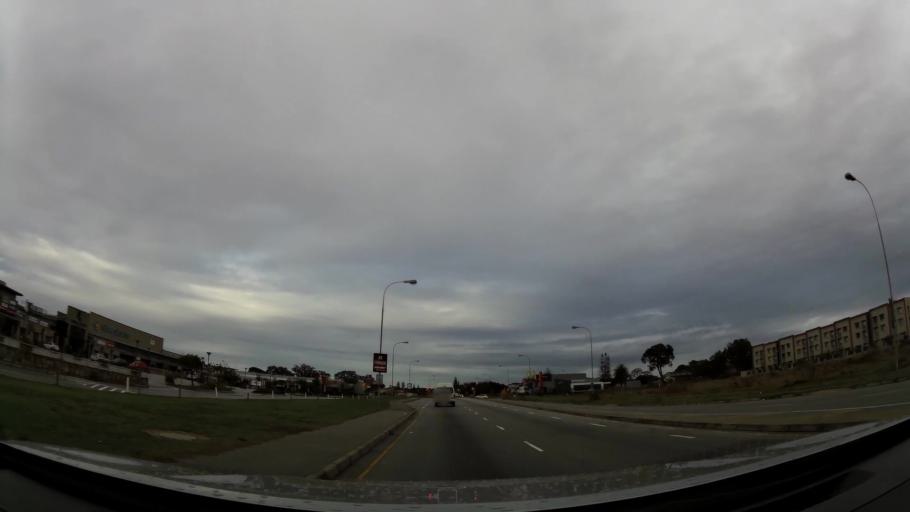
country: ZA
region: Eastern Cape
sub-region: Nelson Mandela Bay Metropolitan Municipality
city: Port Elizabeth
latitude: -33.9827
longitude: 25.5532
